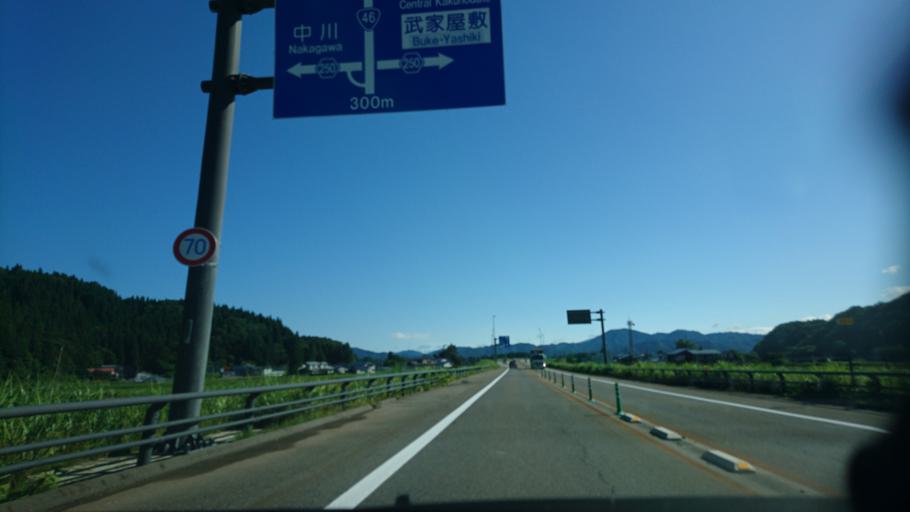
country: JP
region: Akita
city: Kakunodatemachi
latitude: 39.6031
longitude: 140.5530
